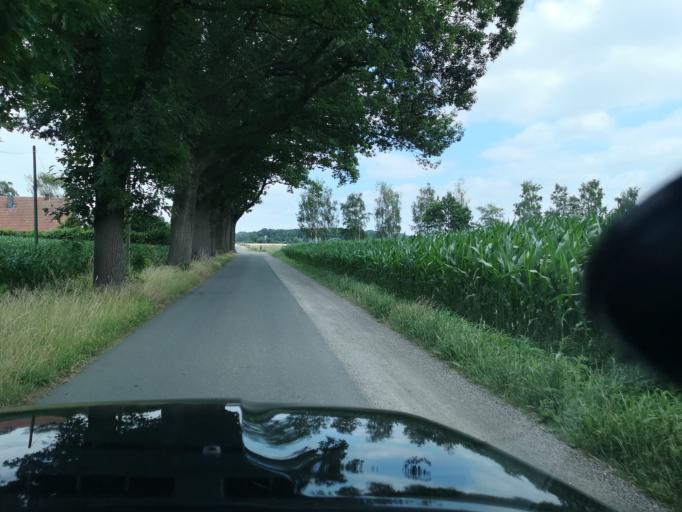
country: DE
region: North Rhine-Westphalia
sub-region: Regierungsbezirk Munster
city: Rhede
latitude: 51.8445
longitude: 6.6805
